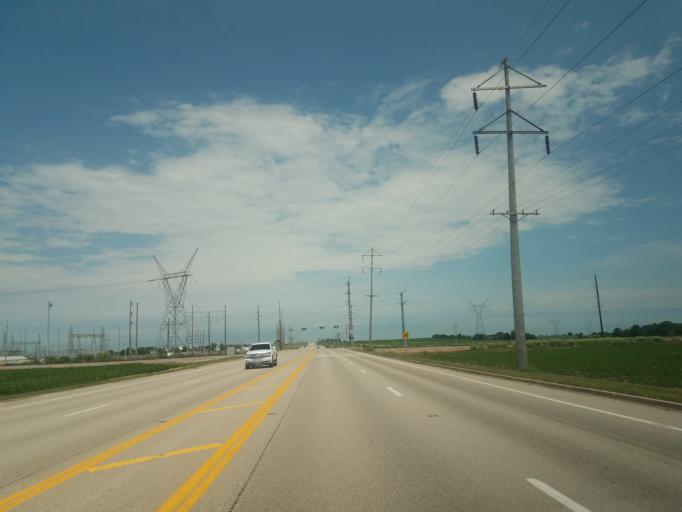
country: US
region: Illinois
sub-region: McLean County
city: Downs
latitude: 40.4498
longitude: -88.9017
